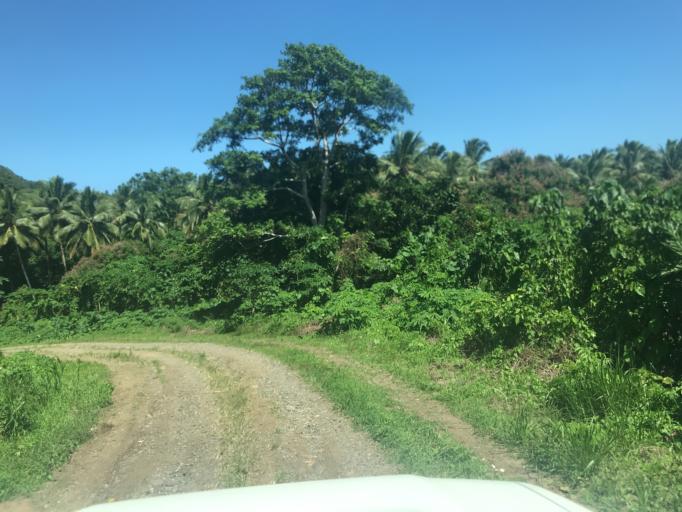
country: VU
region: Sanma
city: Luganville
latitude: -15.6042
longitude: 166.7822
